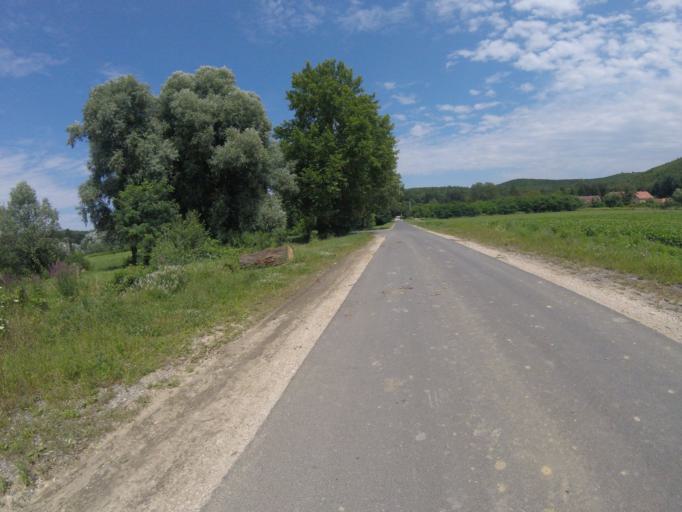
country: HR
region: Medimurska
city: Podturen
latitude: 46.5443
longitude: 16.6085
